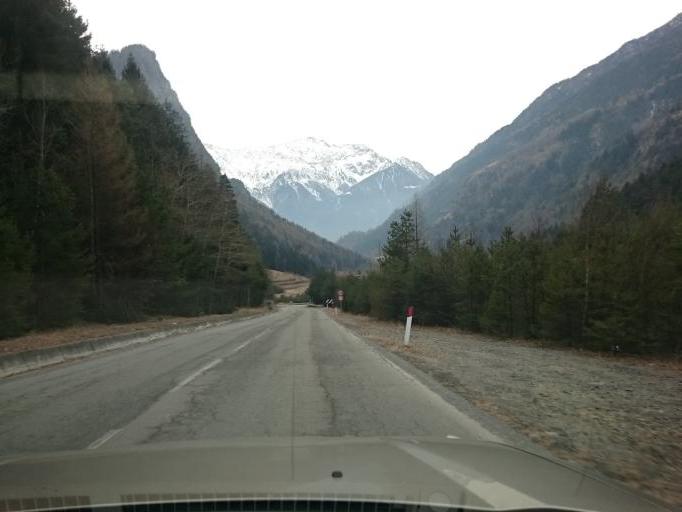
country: IT
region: Lombardy
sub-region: Provincia di Sondrio
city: Sondalo
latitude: 46.3744
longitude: 10.3593
